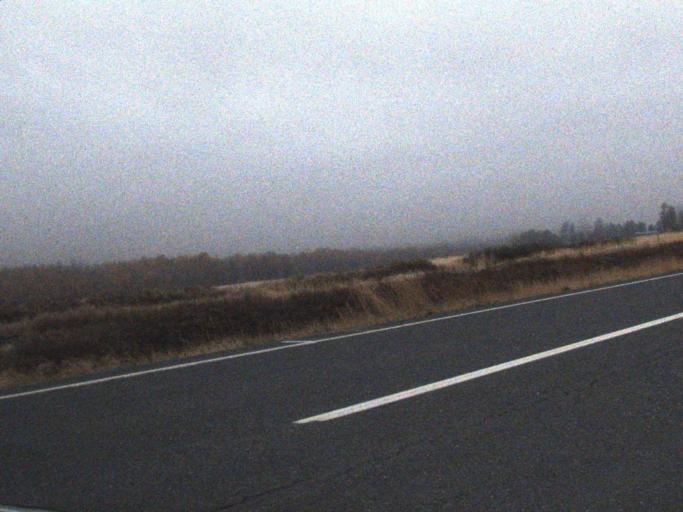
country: US
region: Washington
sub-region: Stevens County
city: Kettle Falls
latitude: 48.6000
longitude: -118.0156
